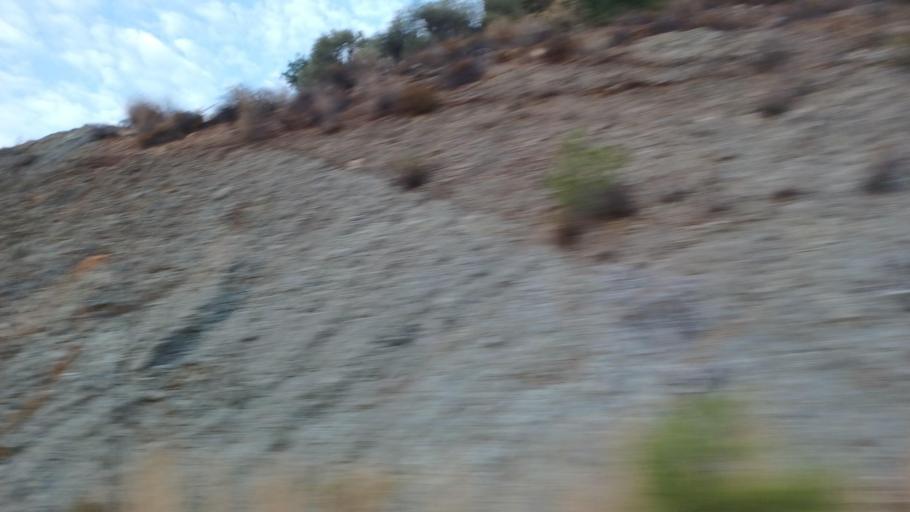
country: CY
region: Limassol
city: Pelendri
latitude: 34.8421
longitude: 32.9519
